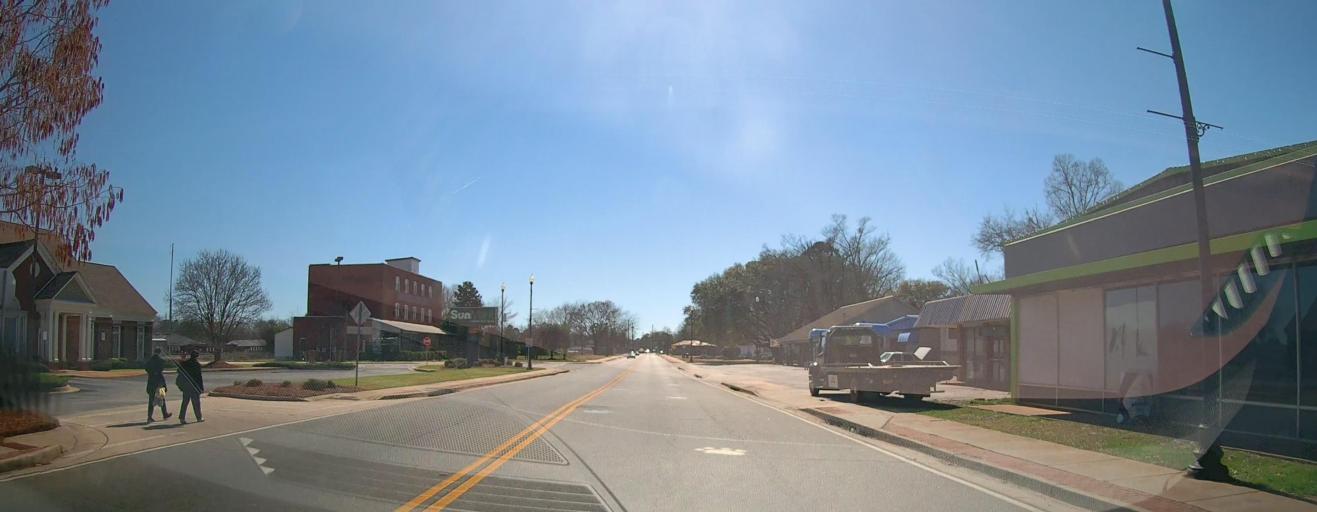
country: US
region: Georgia
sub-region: Peach County
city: Fort Valley
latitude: 32.5524
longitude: -83.8875
